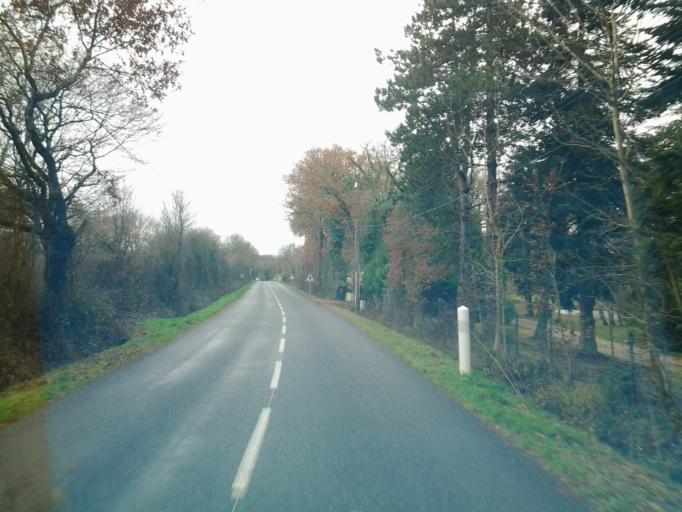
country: FR
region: Pays de la Loire
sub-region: Departement de la Vendee
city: La Roche-sur-Yon
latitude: 46.6739
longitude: -1.3851
